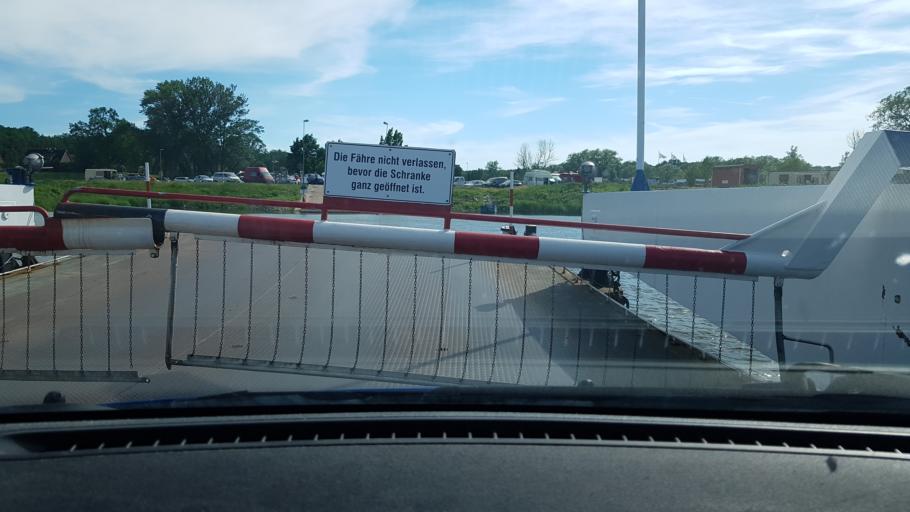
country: DE
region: Lower Saxony
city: Neu Darchau
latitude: 53.2342
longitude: 10.8909
